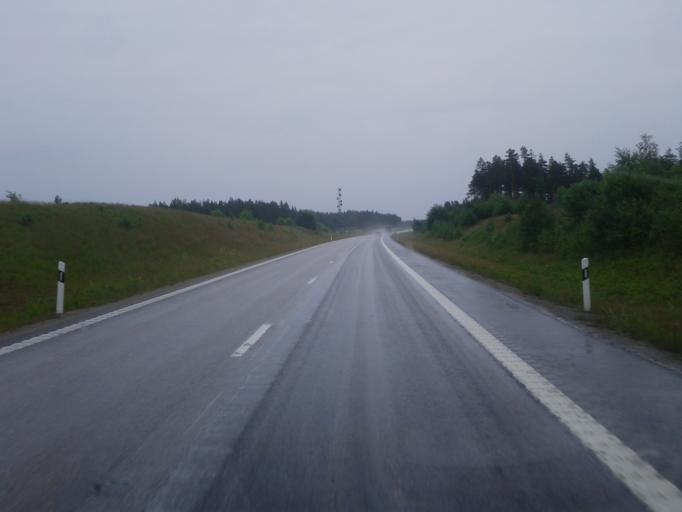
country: SE
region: Uppsala
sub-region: Tierps Kommun
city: Tierp
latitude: 60.2868
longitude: 17.5064
